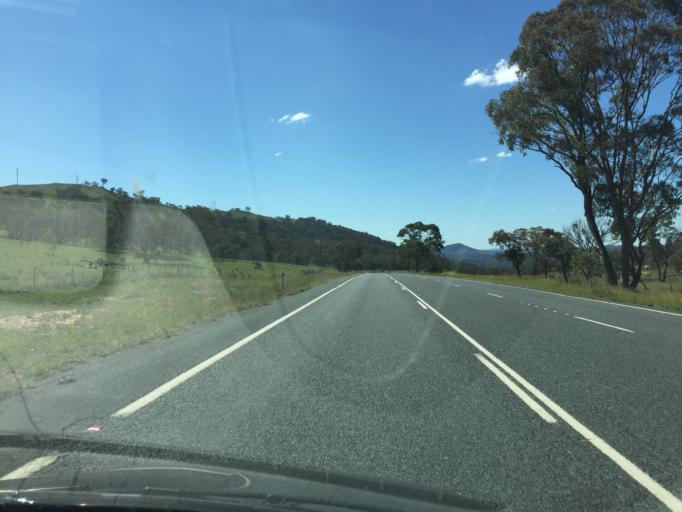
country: AU
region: Australian Capital Territory
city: Macarthur
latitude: -35.4747
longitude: 149.1418
